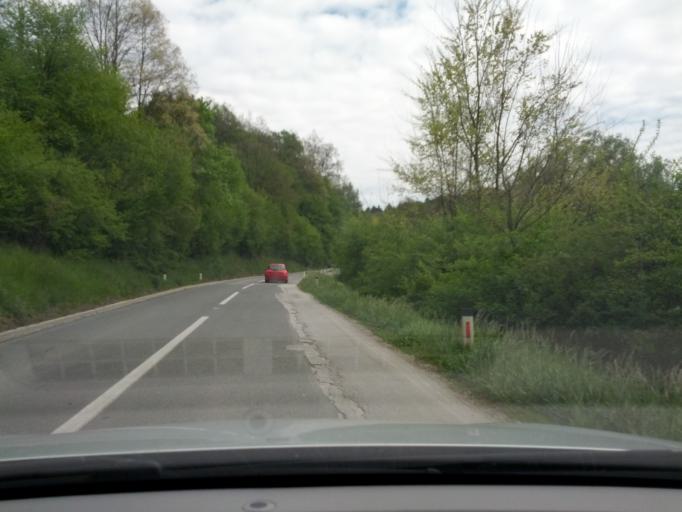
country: SI
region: Smarje pri Jelsah
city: Smarje pri Jelsah
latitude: 46.2295
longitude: 15.5525
